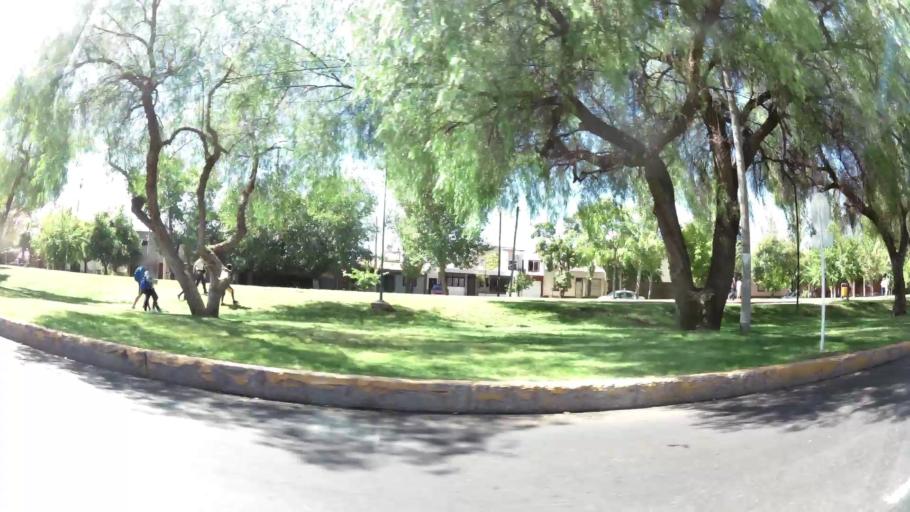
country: AR
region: Mendoza
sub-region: Departamento de Godoy Cruz
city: Godoy Cruz
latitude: -32.9454
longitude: -68.8520
